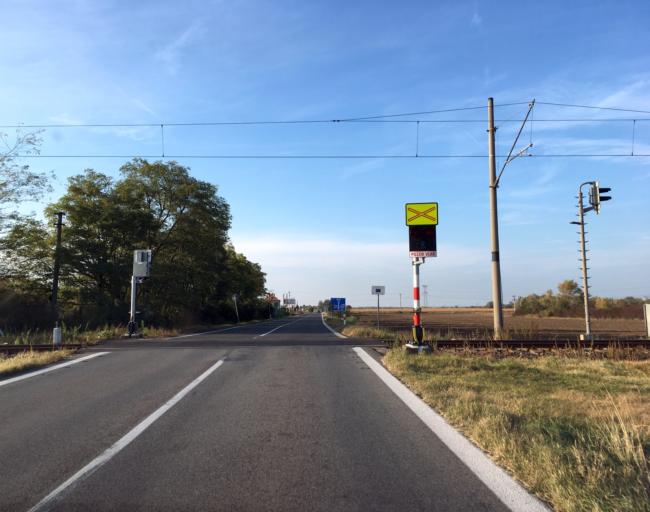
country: SK
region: Nitriansky
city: Surany
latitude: 48.0595
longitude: 18.1020
